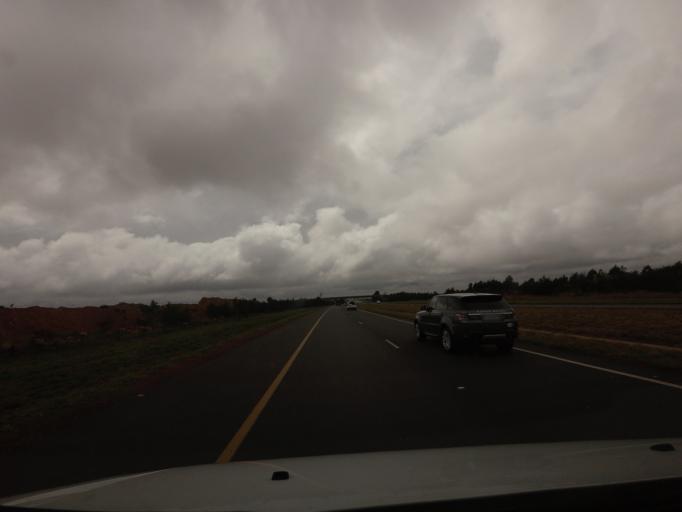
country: ZA
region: Mpumalanga
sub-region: Nkangala District Municipality
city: Middelburg
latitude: -25.8335
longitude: 29.4307
